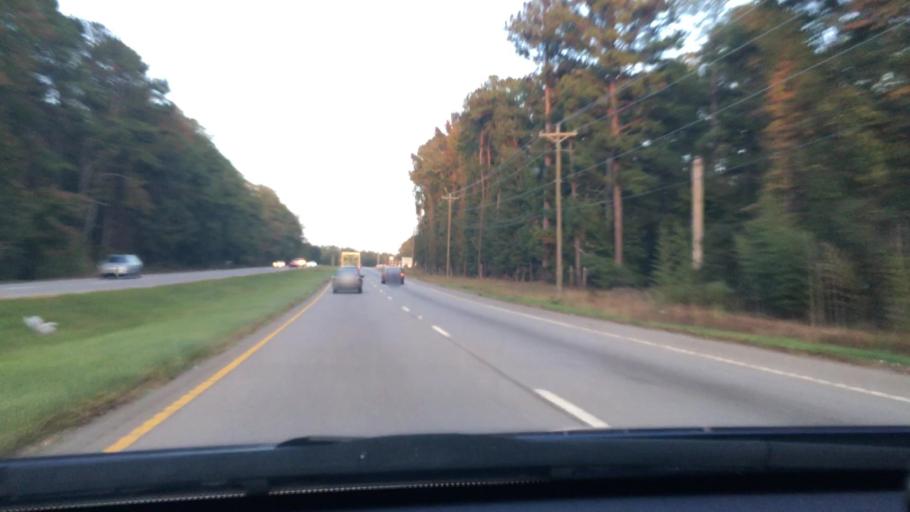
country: US
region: South Carolina
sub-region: Richland County
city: Gadsden
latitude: 33.9410
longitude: -80.7820
